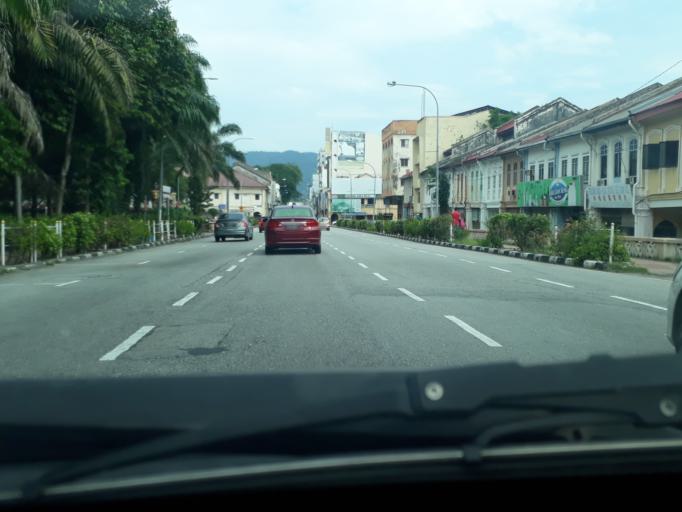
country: MY
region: Perak
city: Ipoh
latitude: 4.5944
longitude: 101.0798
